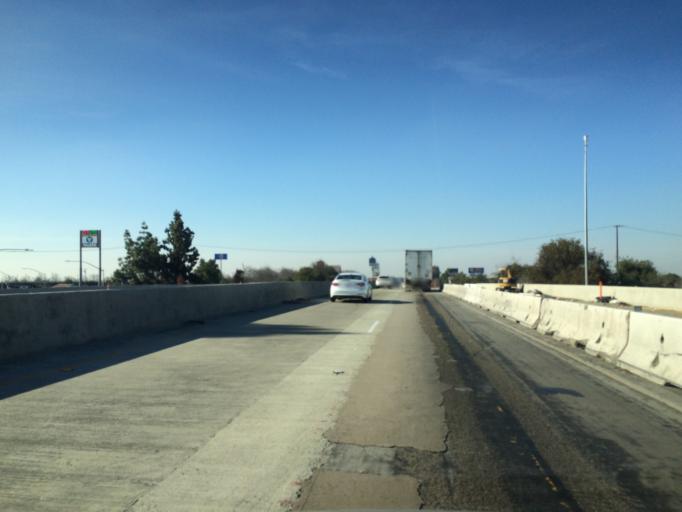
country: US
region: California
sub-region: Fresno County
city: Kingsburg
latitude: 36.5176
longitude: -119.5608
